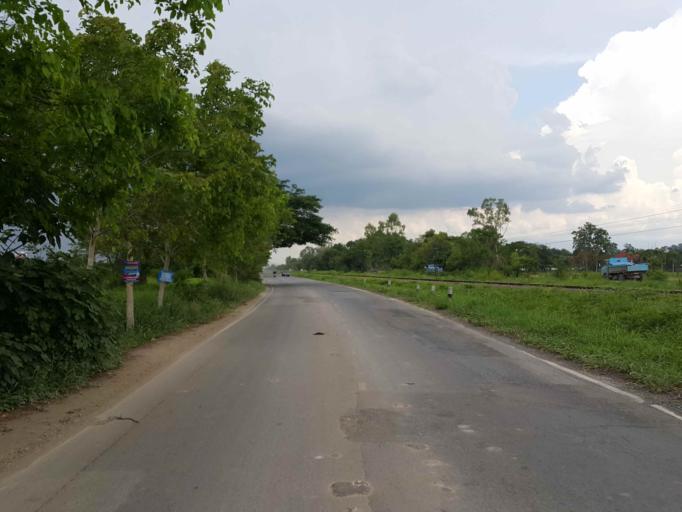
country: TH
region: Chiang Mai
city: Saraphi
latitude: 18.7328
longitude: 99.0322
